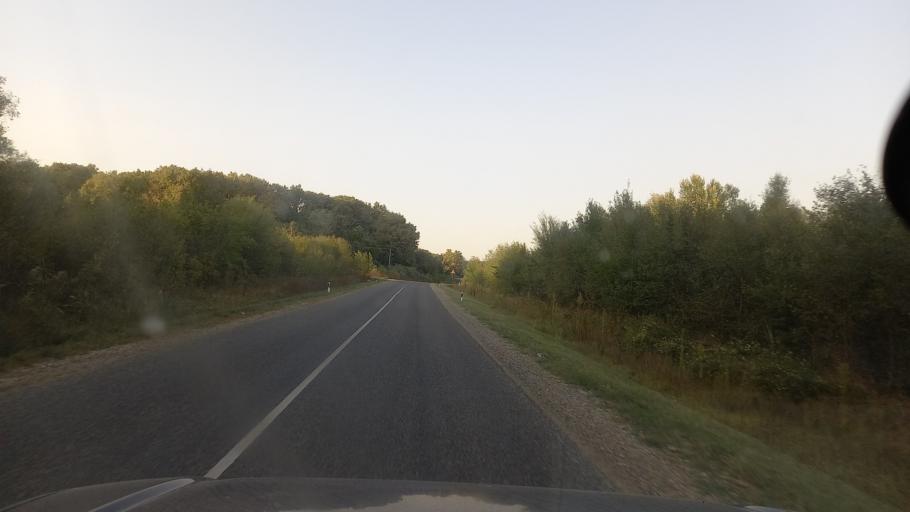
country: RU
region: Krasnodarskiy
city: Smolenskaya
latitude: 44.7510
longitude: 38.7625
